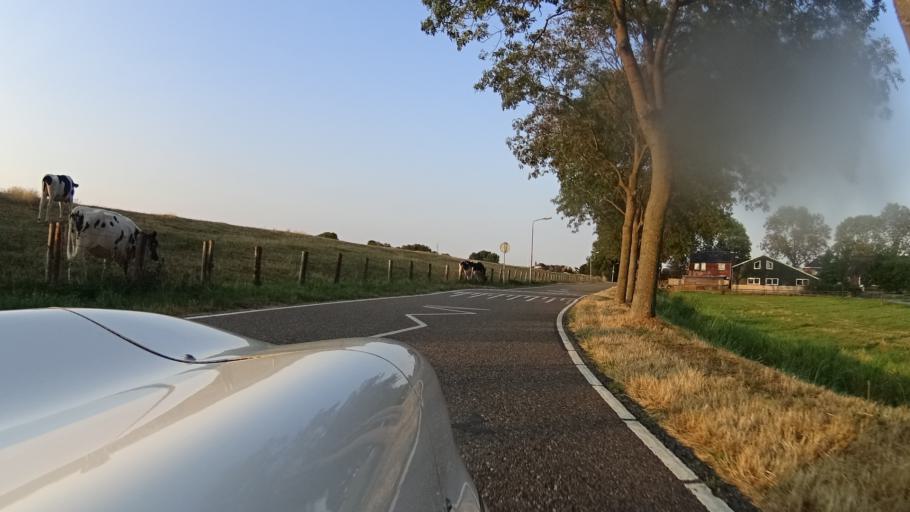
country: NL
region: South Holland
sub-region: Gemeente Kaag en Braassem
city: Oude Wetering
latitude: 52.2163
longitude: 4.6340
